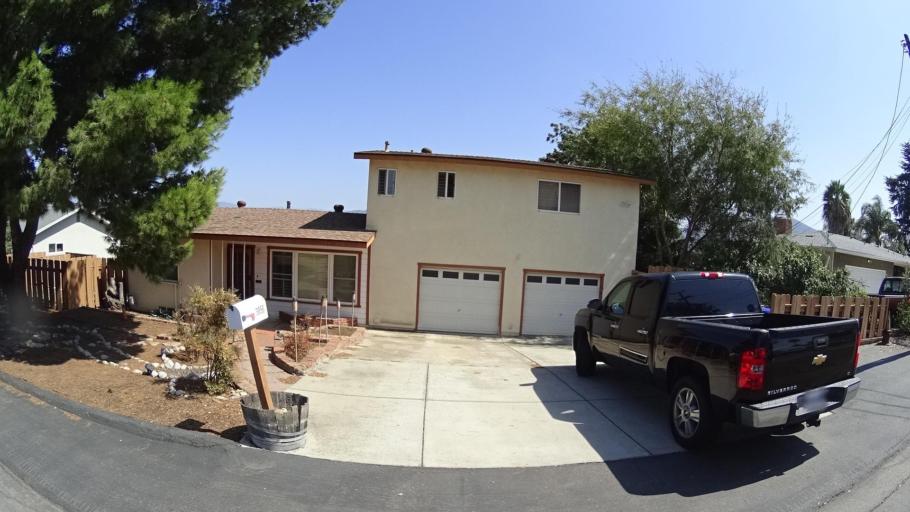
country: US
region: California
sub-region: San Diego County
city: Spring Valley
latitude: 32.7382
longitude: -116.9844
